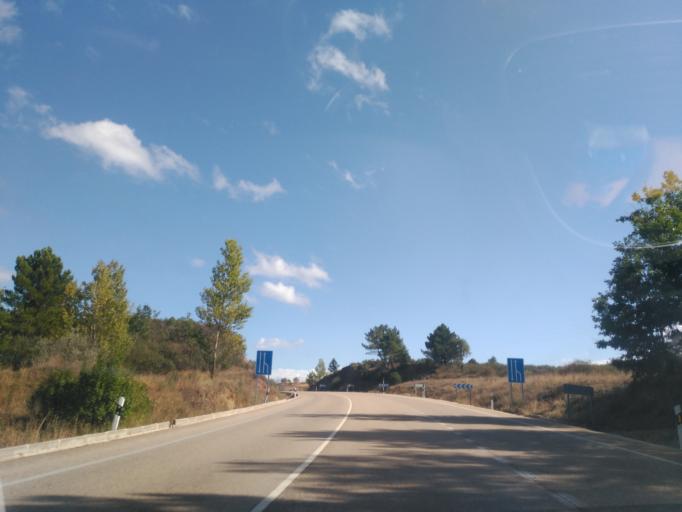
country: ES
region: Castille and Leon
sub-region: Provincia de Burgos
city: Pinilla de los Barruecos
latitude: 41.9001
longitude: -3.2709
